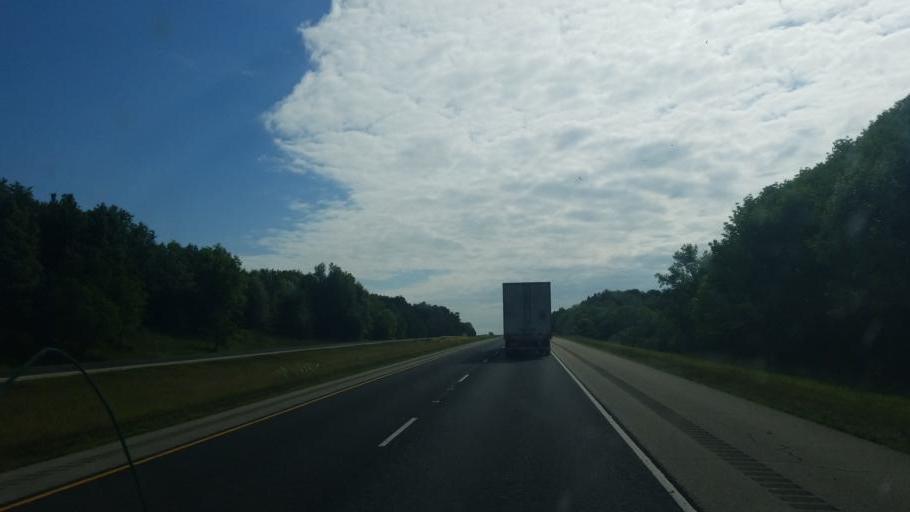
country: US
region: Illinois
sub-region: Clark County
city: Marshall
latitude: 39.3963
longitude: -87.7827
